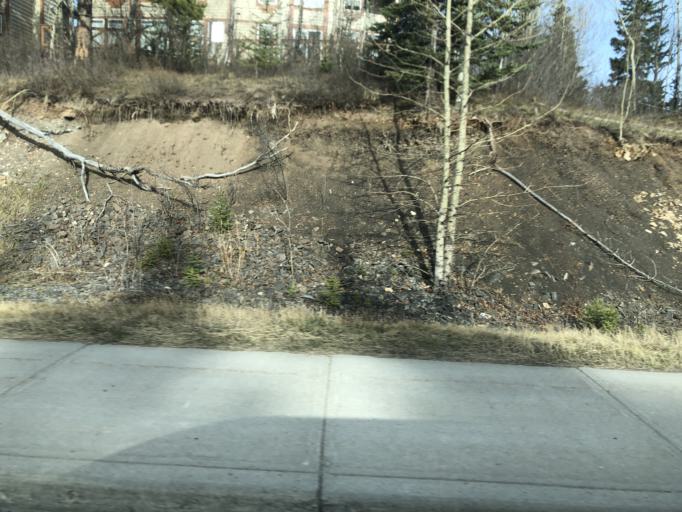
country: CA
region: Alberta
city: Canmore
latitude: 51.0761
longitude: -115.3657
